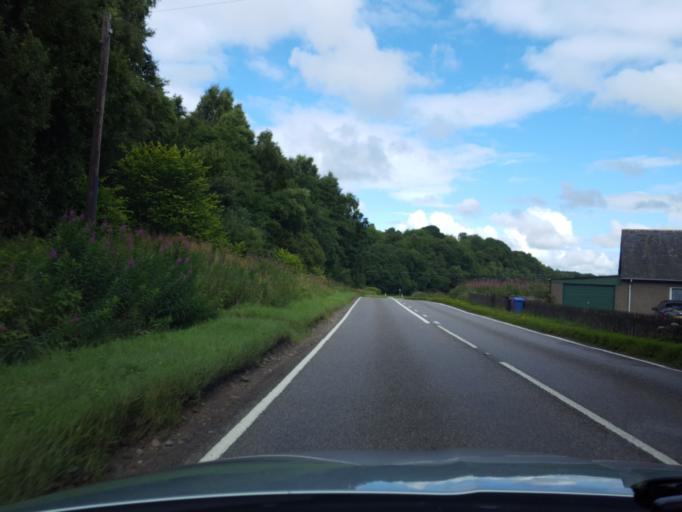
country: GB
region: Scotland
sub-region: Moray
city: Rothes
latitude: 57.5081
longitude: -3.2008
